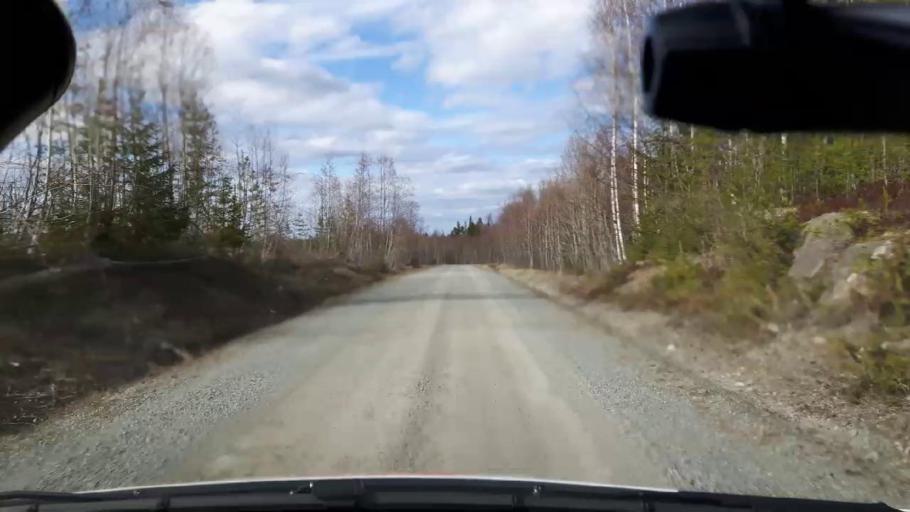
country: SE
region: Jaemtland
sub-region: Bergs Kommun
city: Hoverberg
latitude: 62.7480
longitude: 14.6632
